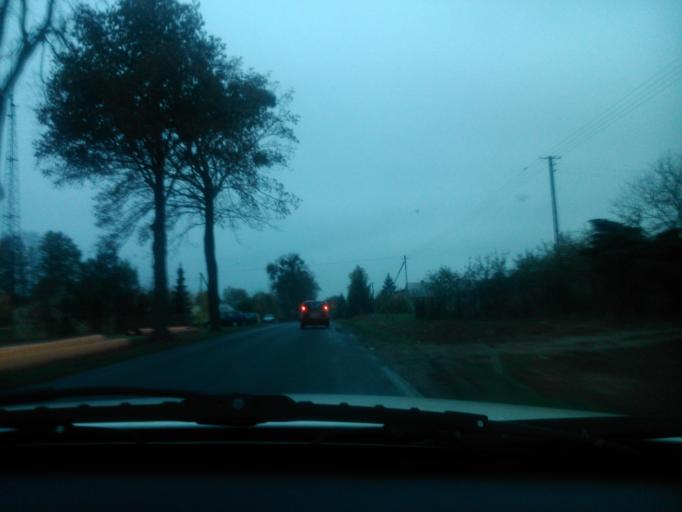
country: PL
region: Kujawsko-Pomorskie
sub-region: Powiat golubsko-dobrzynski
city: Golub-Dobrzyn
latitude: 53.1393
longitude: 18.9957
